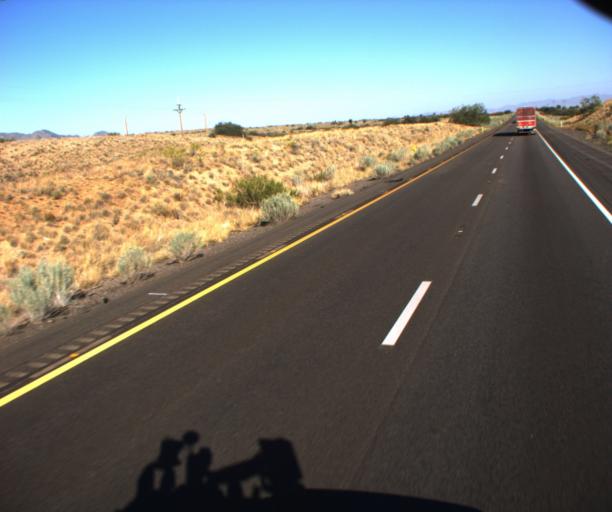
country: US
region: Arizona
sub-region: Mohave County
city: New Kingman-Butler
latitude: 35.1883
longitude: -113.8156
